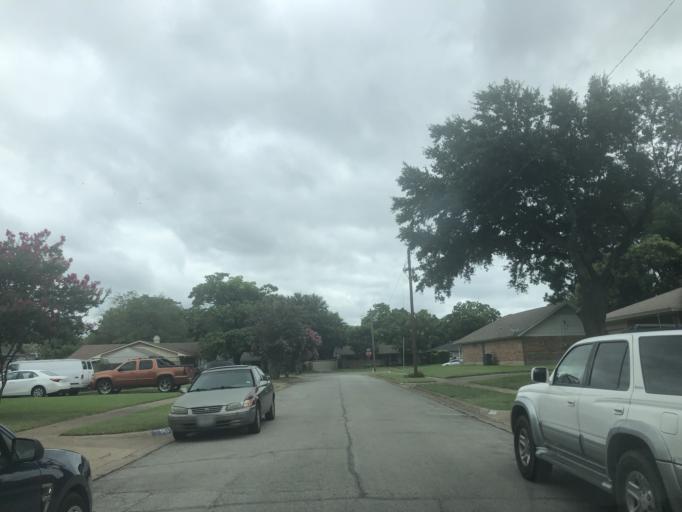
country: US
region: Texas
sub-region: Dallas County
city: Duncanville
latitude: 32.6555
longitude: -96.9155
